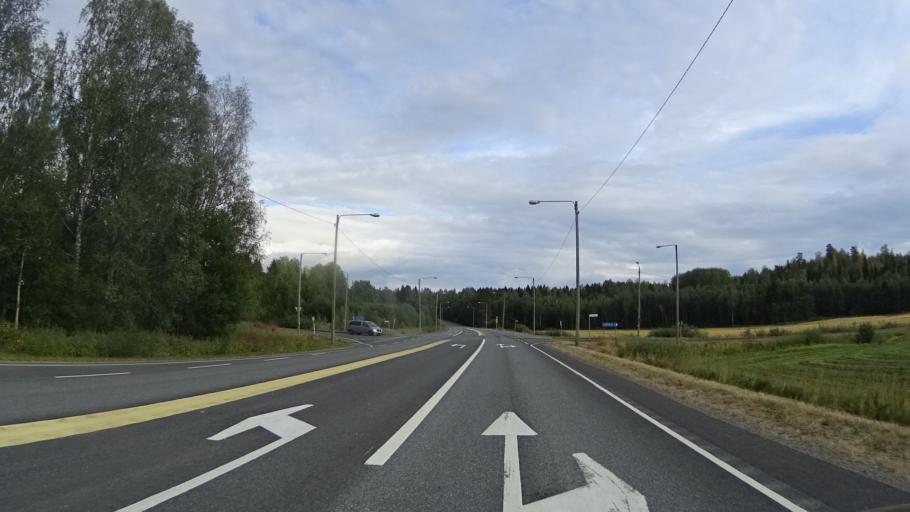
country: FI
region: Haeme
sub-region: Haemeenlinna
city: Parola
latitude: 61.0295
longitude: 24.2785
